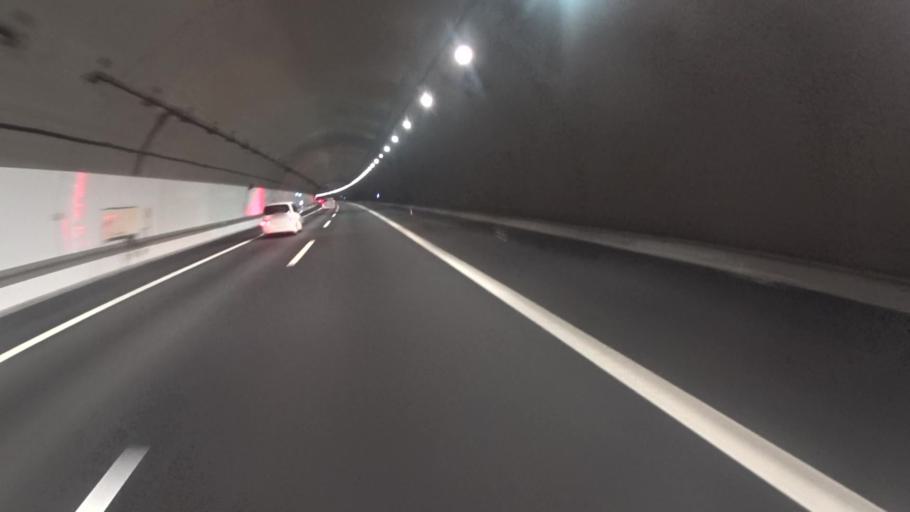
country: JP
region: Shiga Prefecture
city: Kusatsu
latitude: 34.9534
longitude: 136.0125
